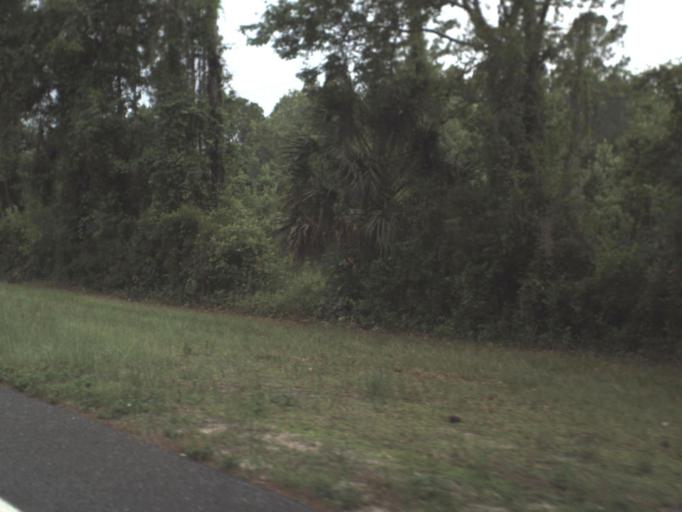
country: US
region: Florida
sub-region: Levy County
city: Bronson
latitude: 29.2987
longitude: -82.7513
